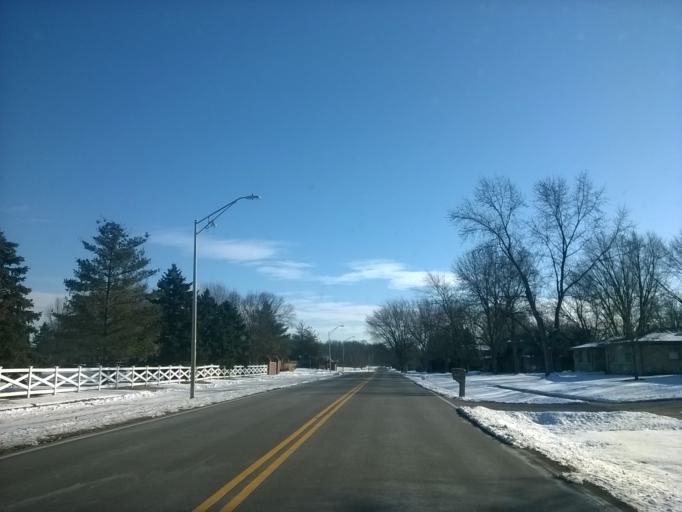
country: US
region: Indiana
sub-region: Hamilton County
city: Carmel
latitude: 39.9470
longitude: -86.0983
